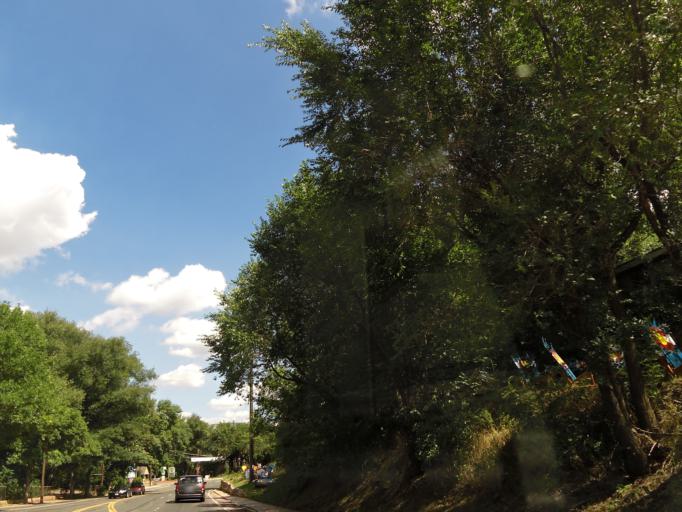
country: US
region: Colorado
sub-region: El Paso County
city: Manitou Springs
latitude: 38.8574
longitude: -104.9050
